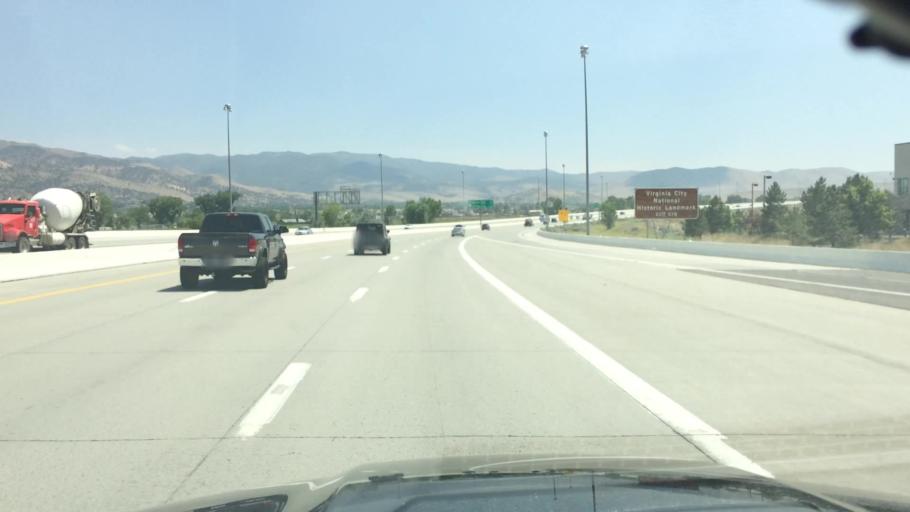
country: US
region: Nevada
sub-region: Washoe County
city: Sparks
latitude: 39.4200
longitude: -119.7484
